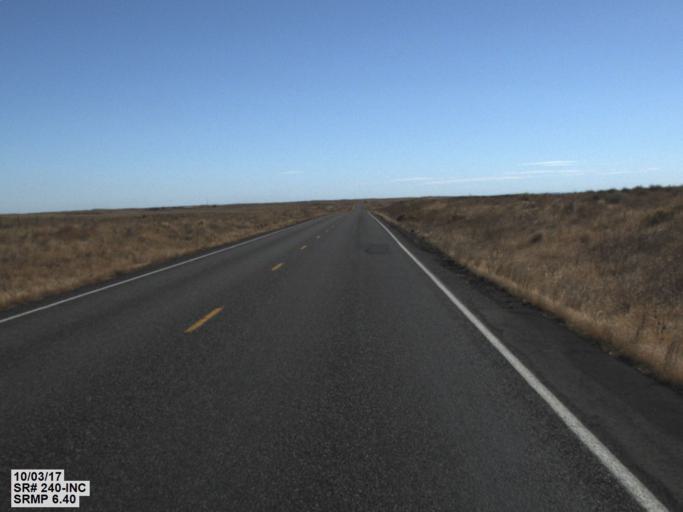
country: US
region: Washington
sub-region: Benton County
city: Benton City
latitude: 46.5086
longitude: -119.6475
